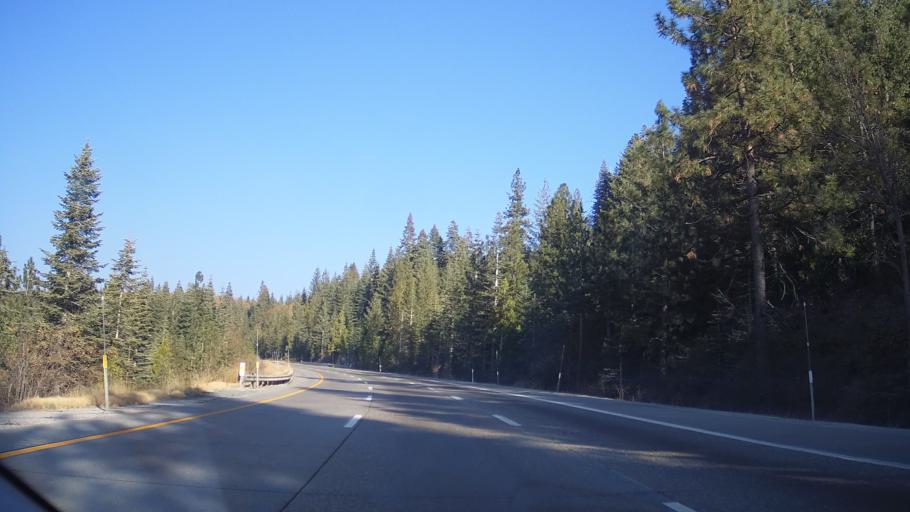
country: US
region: California
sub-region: Placer County
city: Foresthill
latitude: 39.2544
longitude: -120.7345
